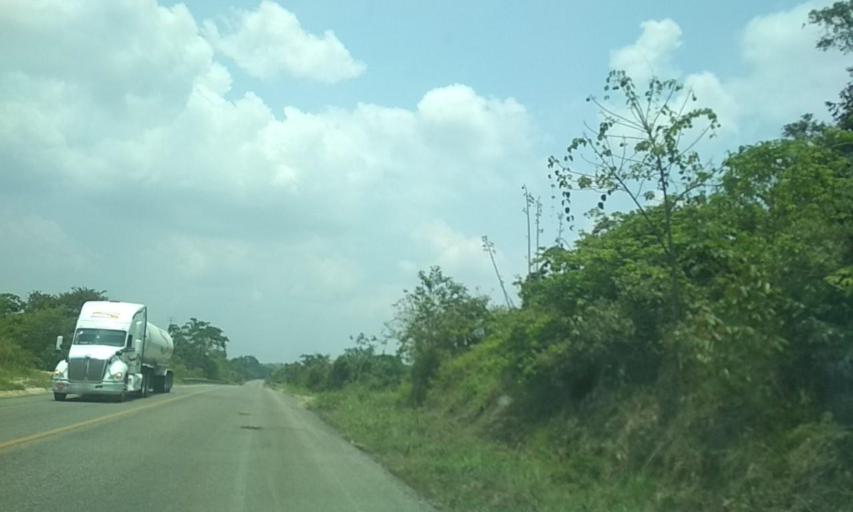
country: MX
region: Tabasco
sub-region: Huimanguillo
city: Francisco Rueda
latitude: 17.6462
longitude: -93.8291
